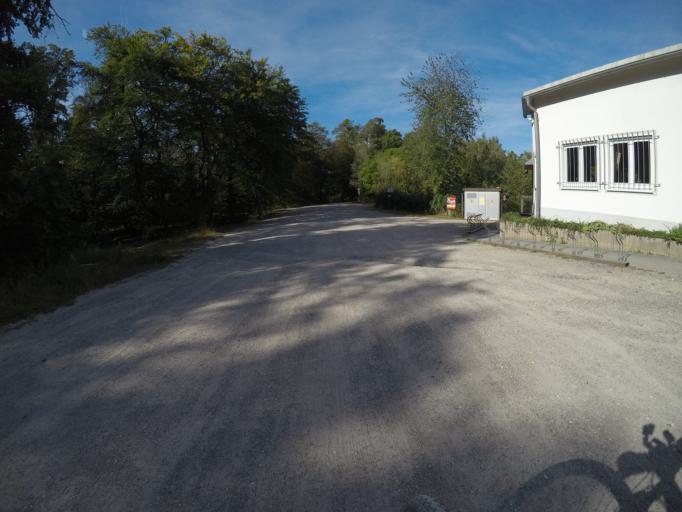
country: DE
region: Baden-Wuerttemberg
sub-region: Karlsruhe Region
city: Kronau
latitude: 49.2377
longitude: 8.6098
